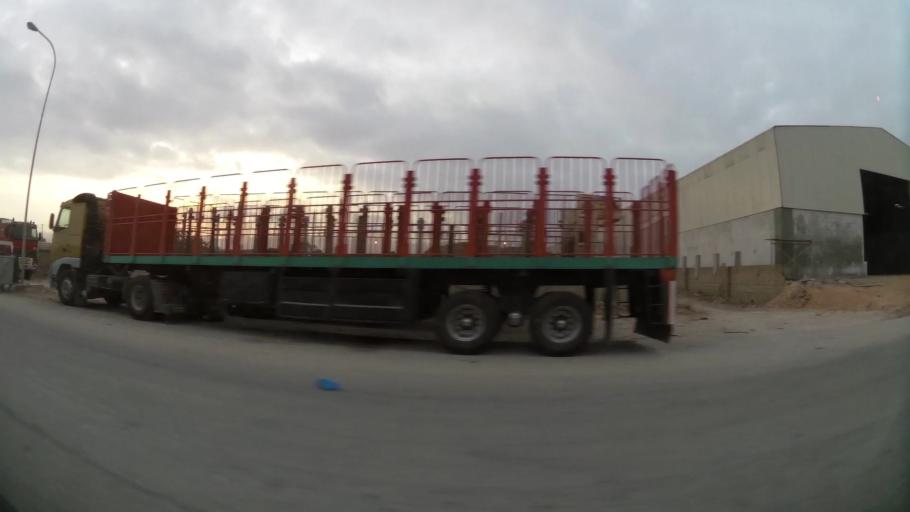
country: OM
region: Zufar
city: Salalah
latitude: 17.0265
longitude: 54.0375
